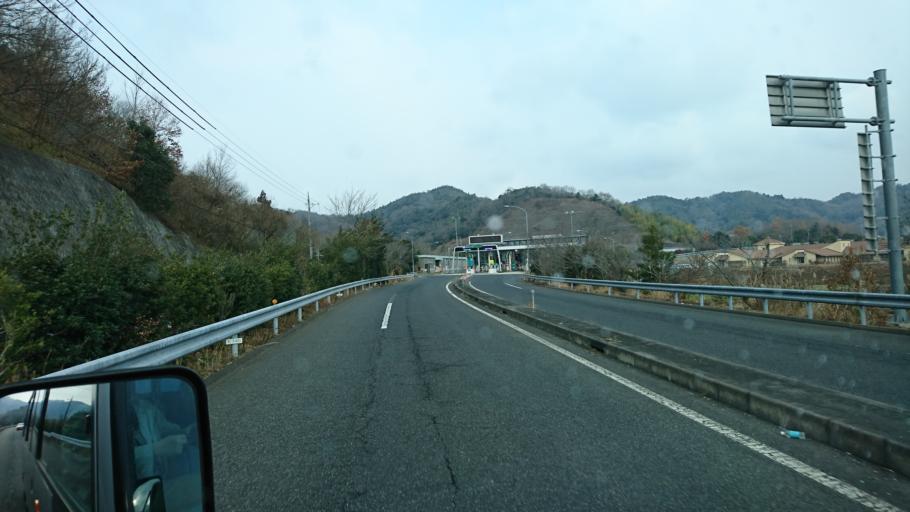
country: JP
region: Hyogo
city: Kakogawacho-honmachi
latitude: 34.8460
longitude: 134.8329
